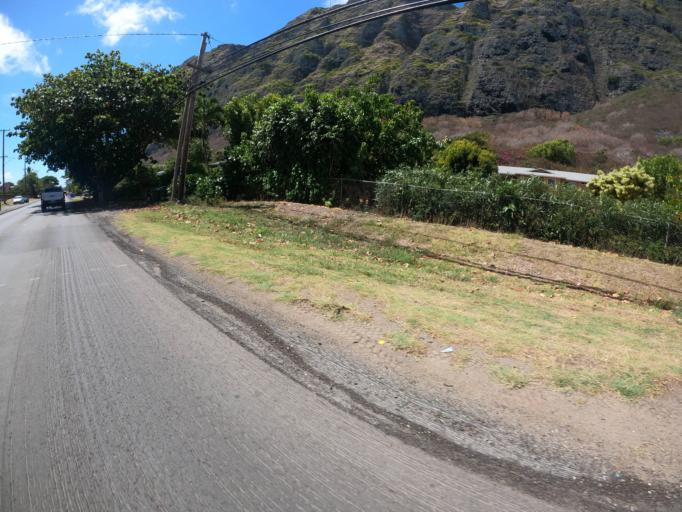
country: US
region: Hawaii
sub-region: Honolulu County
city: Waimanalo Beach
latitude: 21.3254
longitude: -157.6838
